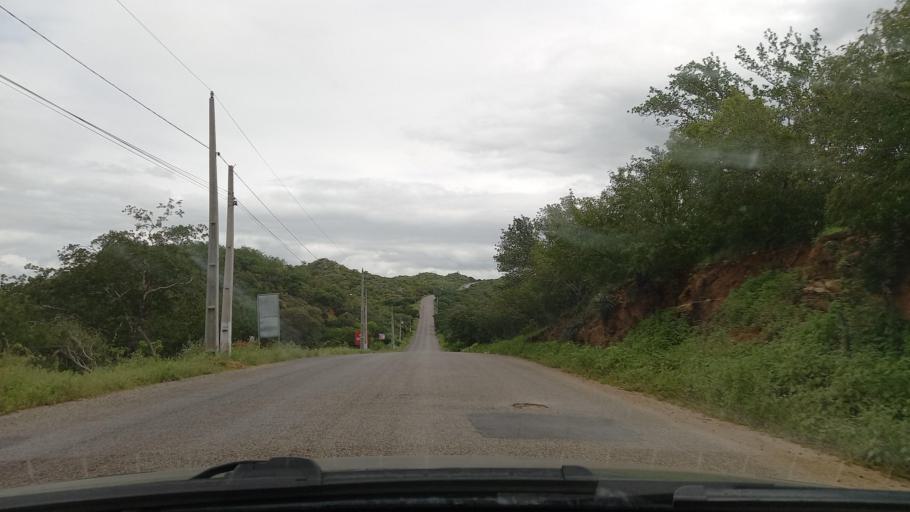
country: BR
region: Sergipe
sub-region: Caninde De Sao Francisco
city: Caninde de Sao Francisco
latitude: -9.6327
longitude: -37.7762
